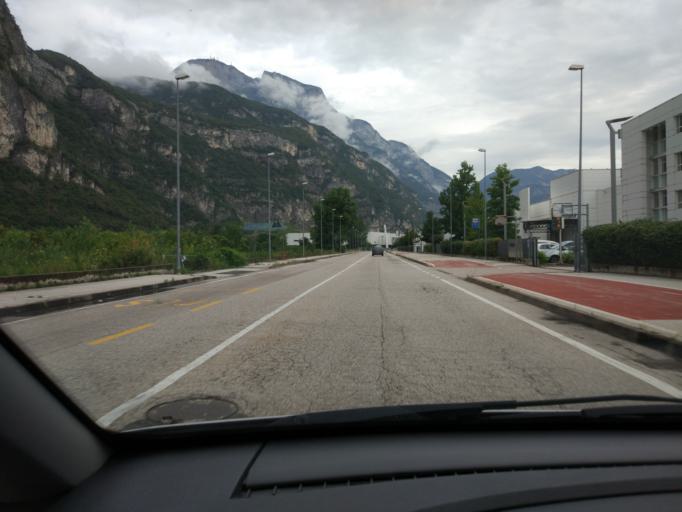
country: IT
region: Trentino-Alto Adige
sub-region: Provincia di Trento
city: Cadine
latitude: 46.1019
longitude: 11.0949
